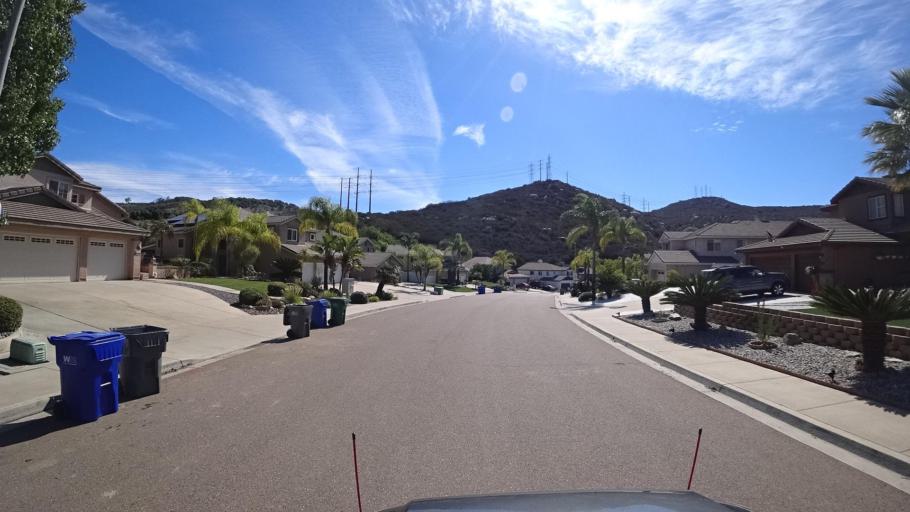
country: US
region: California
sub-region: San Diego County
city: Granite Hills
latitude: 32.8291
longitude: -116.8907
